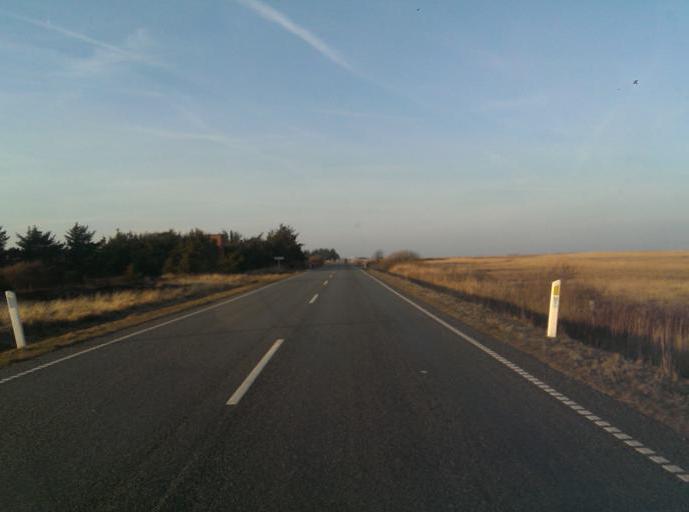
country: DK
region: Central Jutland
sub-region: Ringkobing-Skjern Kommune
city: Hvide Sande
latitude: 55.8475
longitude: 8.1751
